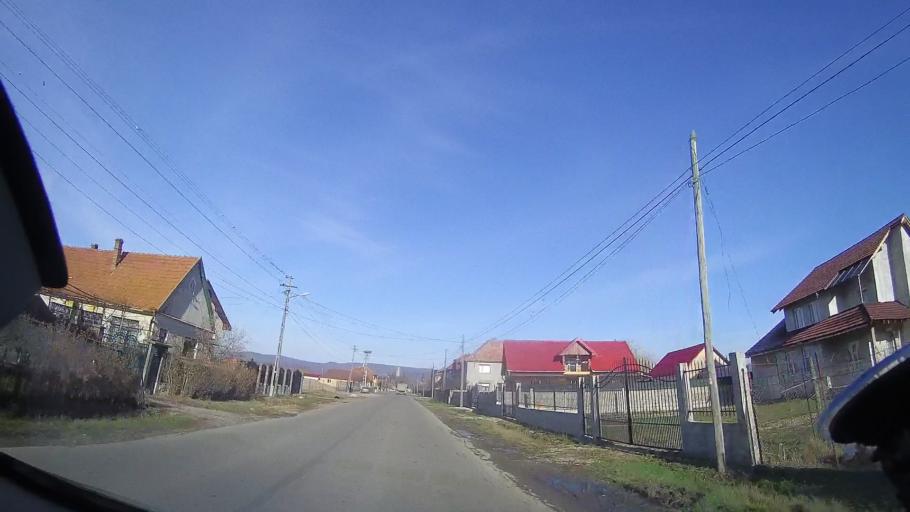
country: RO
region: Bihor
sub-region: Comuna Astileu
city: Astileu
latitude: 47.0330
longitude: 22.3896
